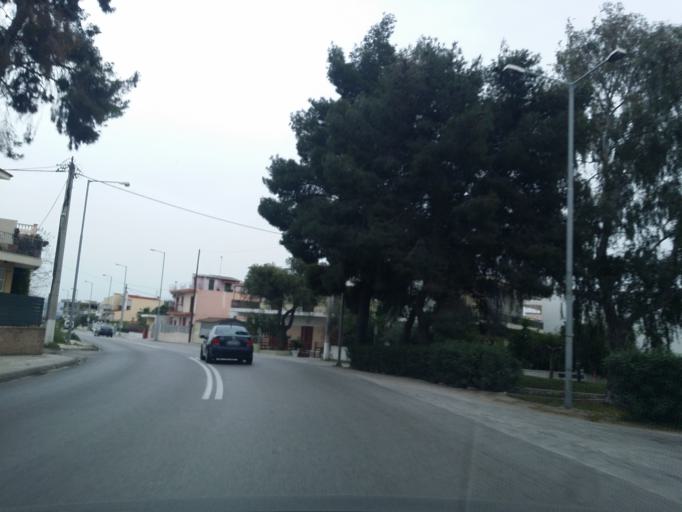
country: GR
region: Attica
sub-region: Nomarchia Dytikis Attikis
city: Mandra
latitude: 38.0786
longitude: 23.4949
